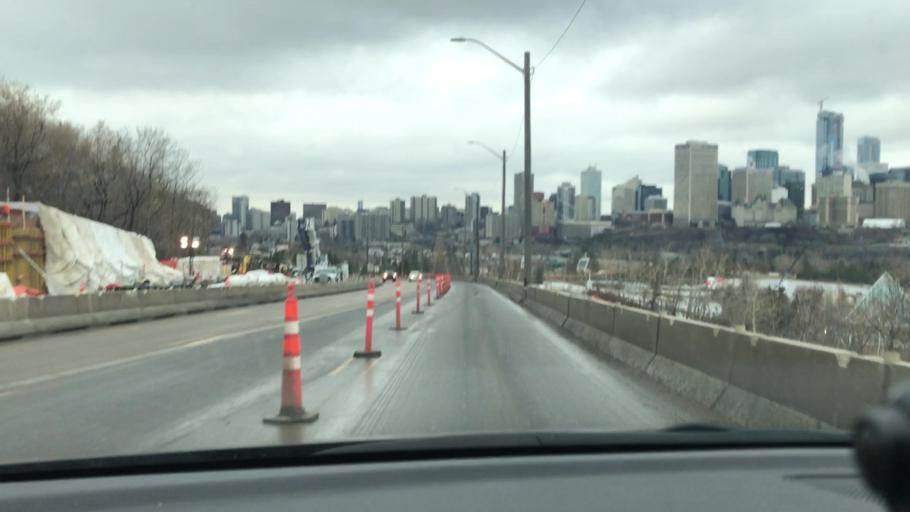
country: CA
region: Alberta
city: Edmonton
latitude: 53.5327
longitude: -113.4738
